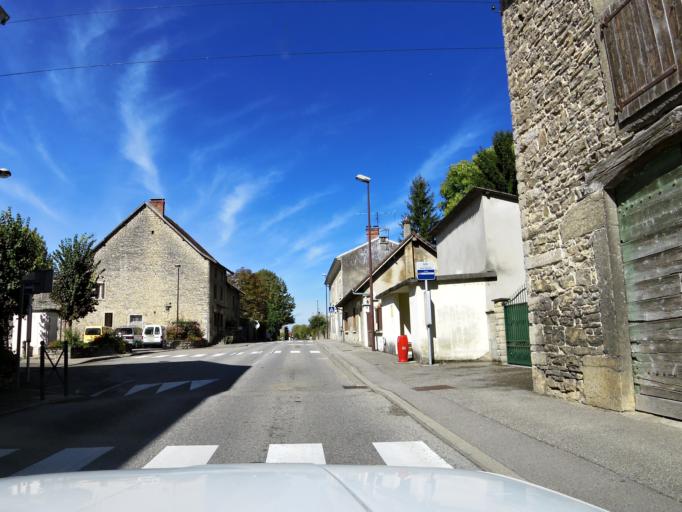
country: FR
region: Rhone-Alpes
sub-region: Departement de l'Ain
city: Sault-Brenaz
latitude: 45.8621
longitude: 5.3984
